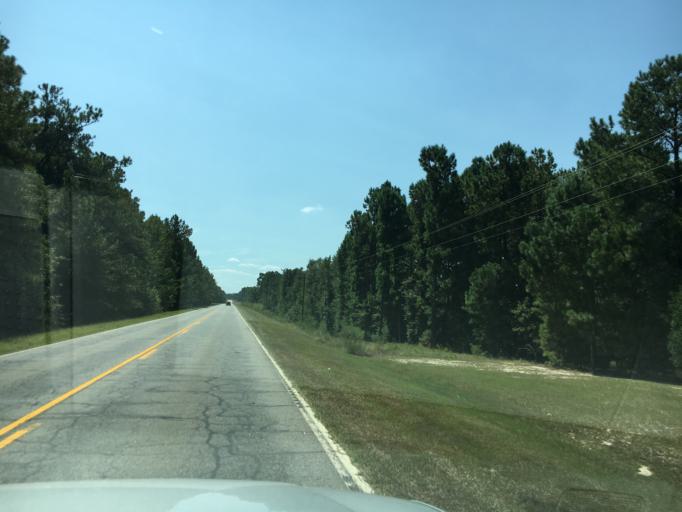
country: US
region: South Carolina
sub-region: Lexington County
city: Batesburg
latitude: 33.7709
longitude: -81.6408
